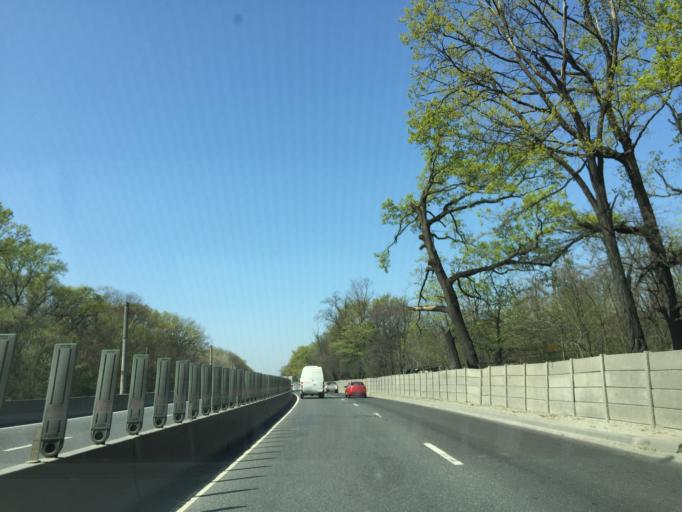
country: RO
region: Ilfov
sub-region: Comuna Tunari
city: Tunari
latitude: 44.5392
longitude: 26.1208
